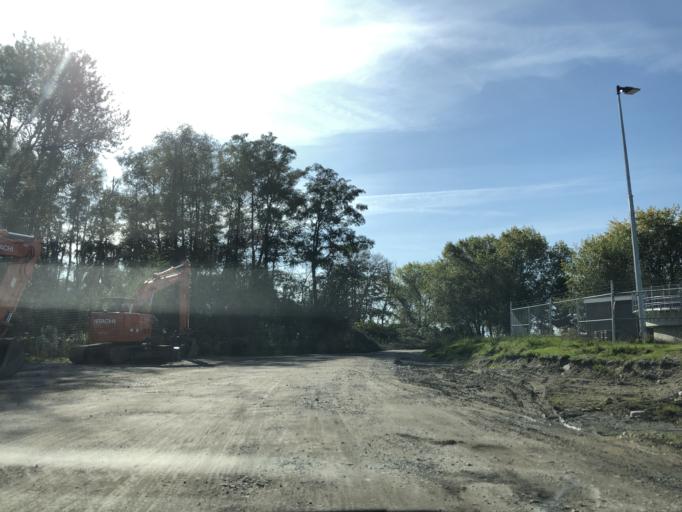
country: CA
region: British Columbia
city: Richmond
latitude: 49.2174
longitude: -123.1988
